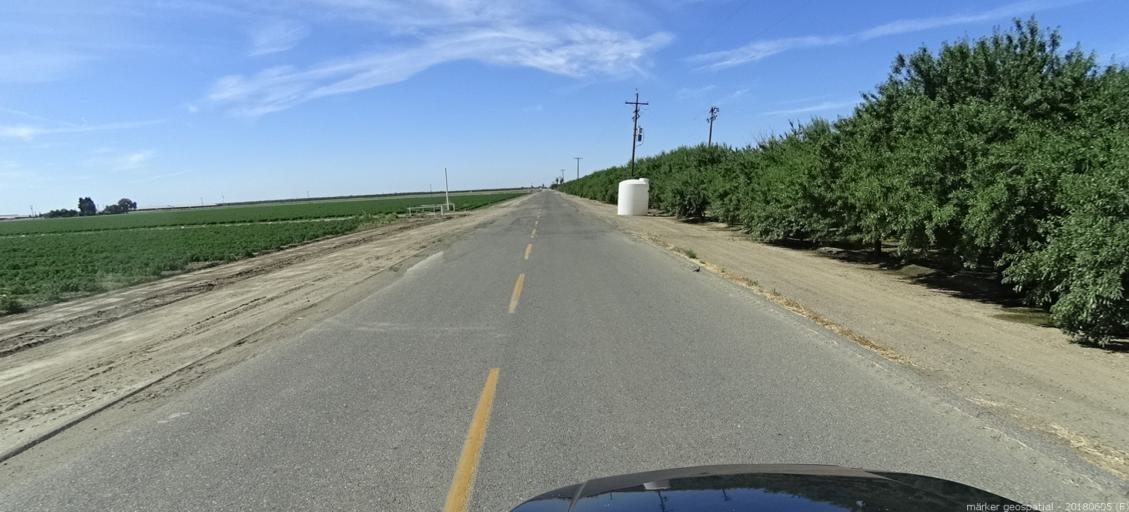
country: US
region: California
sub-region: Madera County
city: Chowchilla
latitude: 37.1169
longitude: -120.4008
